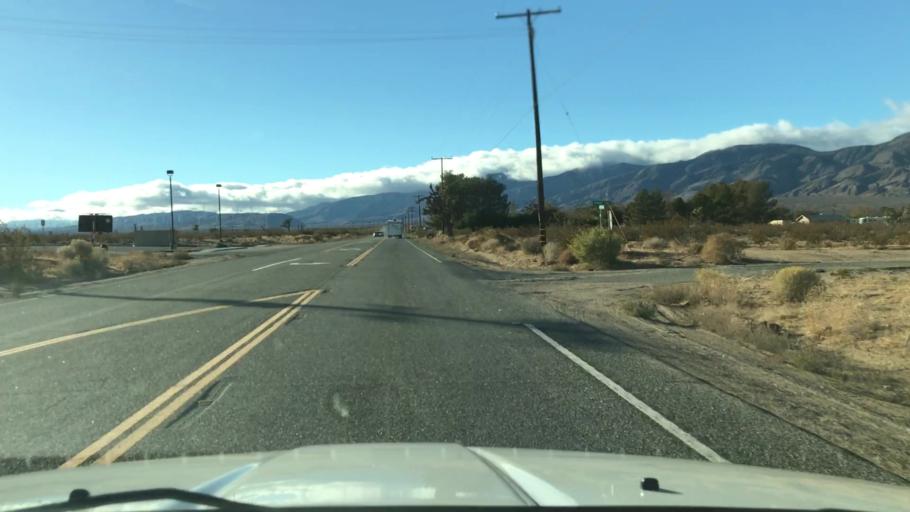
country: US
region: California
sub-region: Kern County
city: Mojave
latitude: 35.1255
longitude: -118.1103
